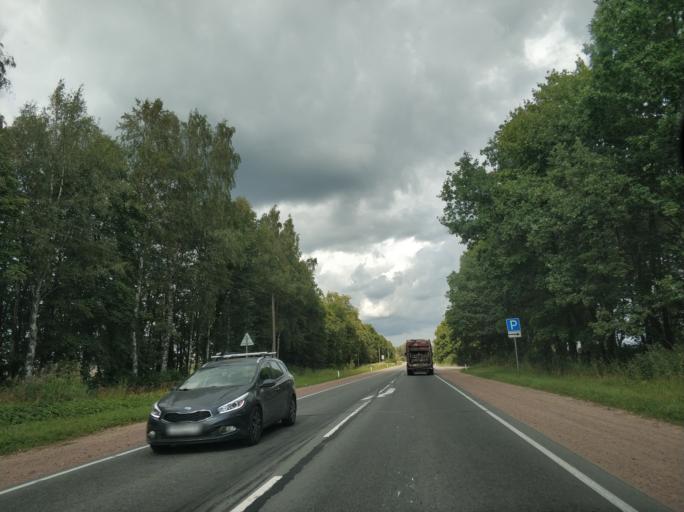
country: RU
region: Leningrad
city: Romanovka
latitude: 60.0624
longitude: 30.7419
